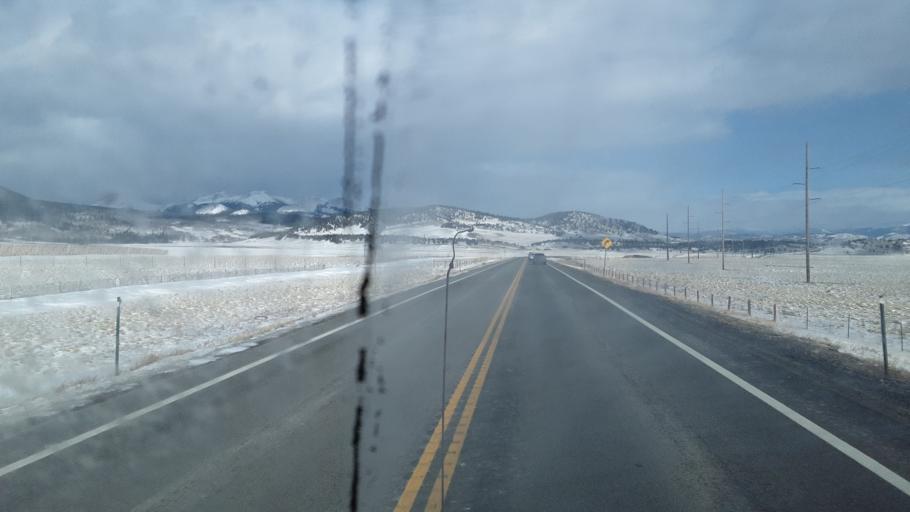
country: US
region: Colorado
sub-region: Park County
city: Fairplay
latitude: 39.2820
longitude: -105.9146
